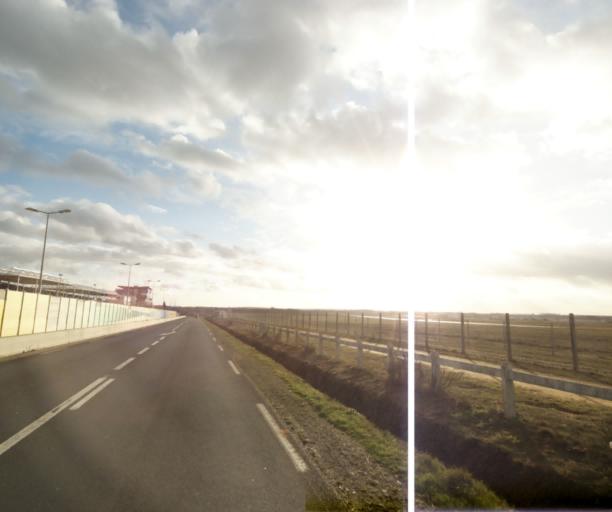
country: FR
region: Pays de la Loire
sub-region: Departement de la Sarthe
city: Arnage
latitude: 47.9548
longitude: 0.2067
